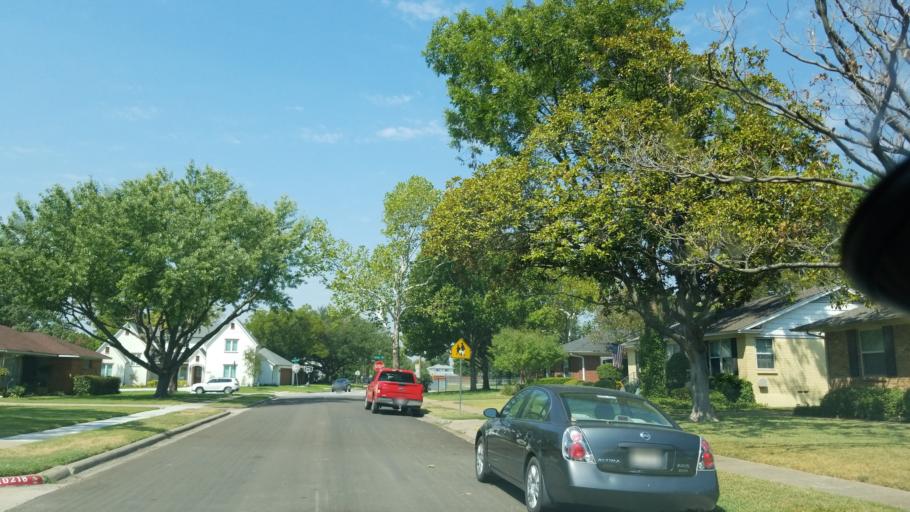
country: US
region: Texas
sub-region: Dallas County
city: Richardson
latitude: 32.8750
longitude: -96.7077
